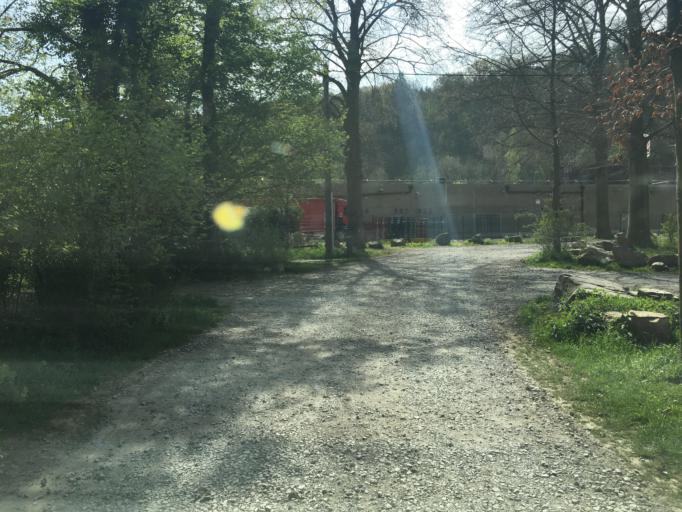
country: BE
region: Wallonia
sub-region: Province de Liege
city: Aywaille
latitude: 50.4776
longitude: 5.6902
